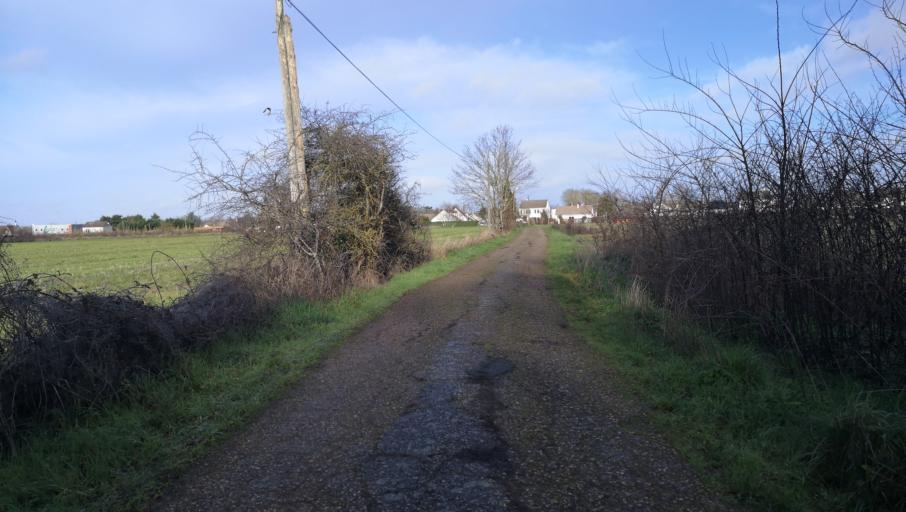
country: FR
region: Centre
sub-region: Departement du Loiret
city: Saint-Pryve-Saint-Mesmin
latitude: 47.8729
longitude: 1.8674
